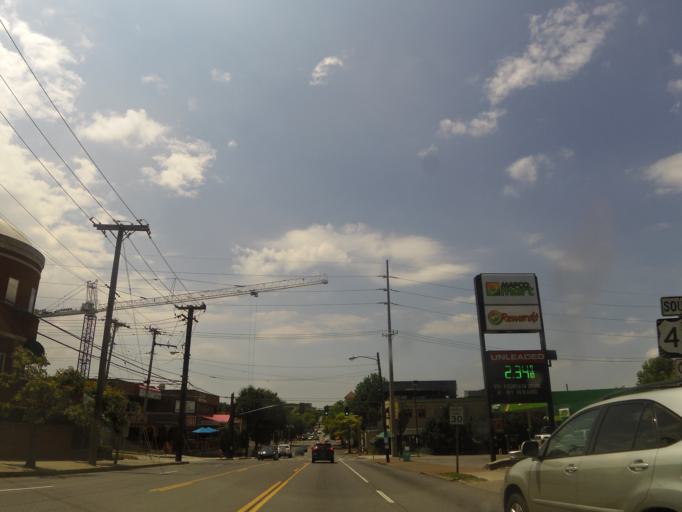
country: US
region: Tennessee
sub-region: Davidson County
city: Nashville
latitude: 36.1393
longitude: -86.8006
